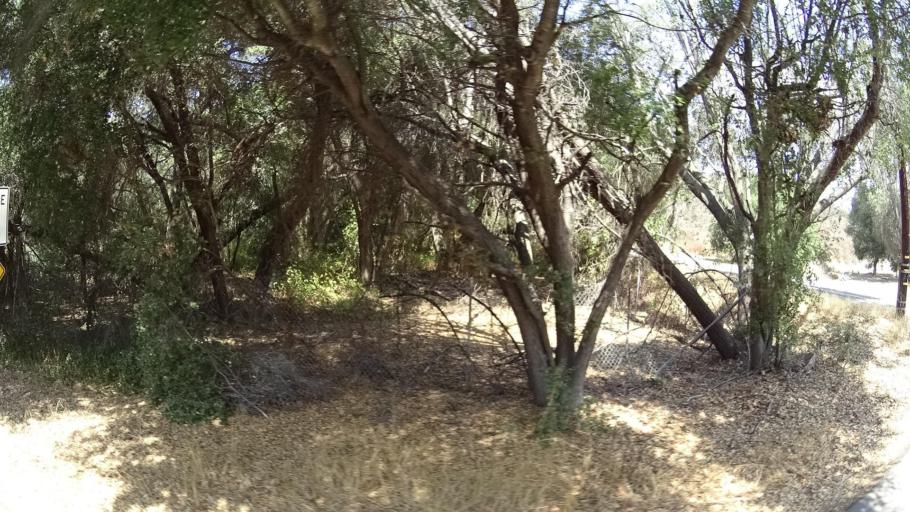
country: US
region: California
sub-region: San Diego County
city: Escondido
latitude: 33.1713
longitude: -117.1031
